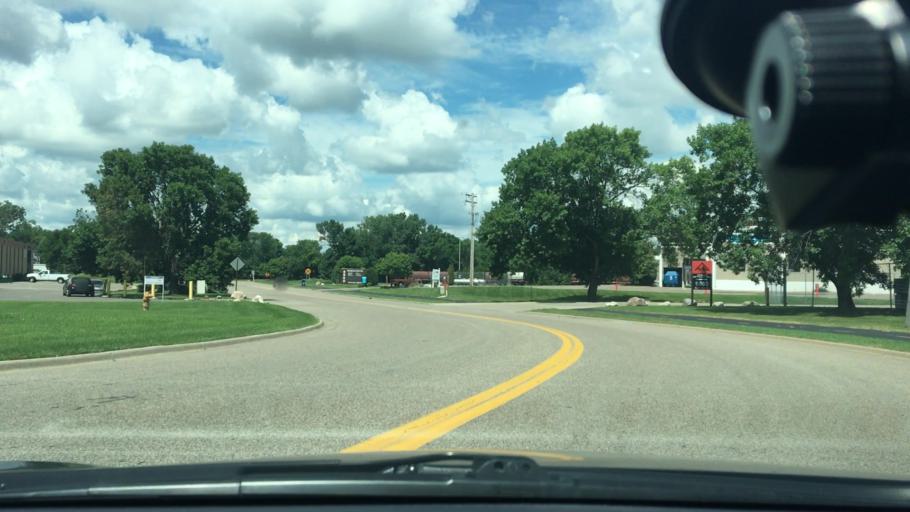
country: US
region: Minnesota
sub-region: Hennepin County
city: New Hope
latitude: 44.9934
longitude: -93.4044
